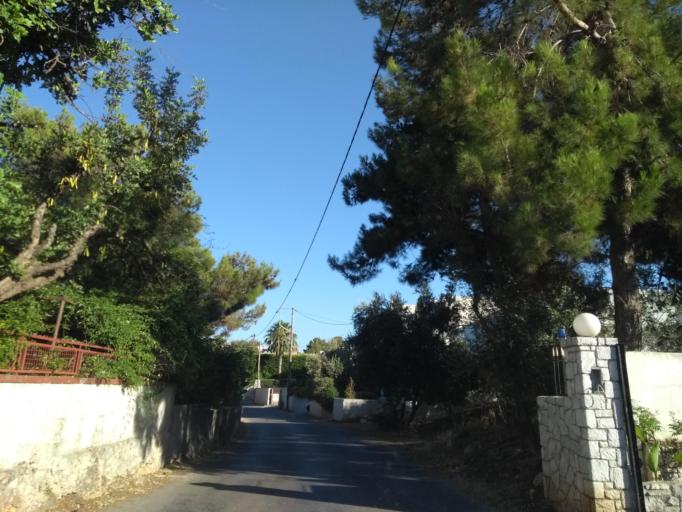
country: GR
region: Crete
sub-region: Nomos Chanias
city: Pithari
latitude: 35.5211
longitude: 24.0779
